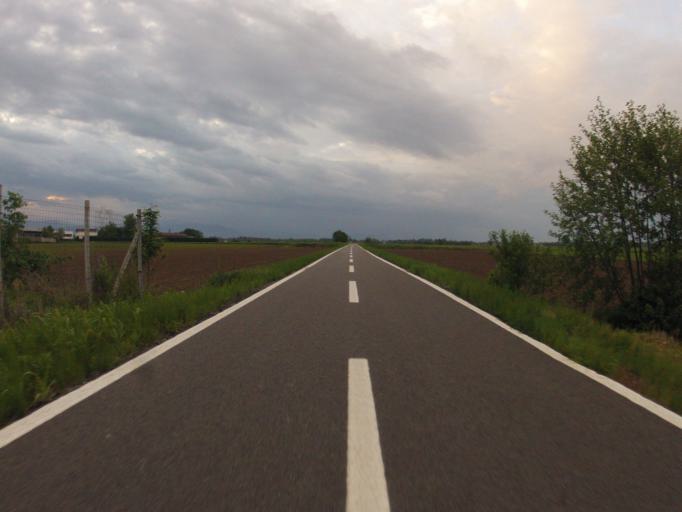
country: IT
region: Piedmont
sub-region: Provincia di Torino
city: Villafranca Piemonte
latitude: 44.7937
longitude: 7.5072
